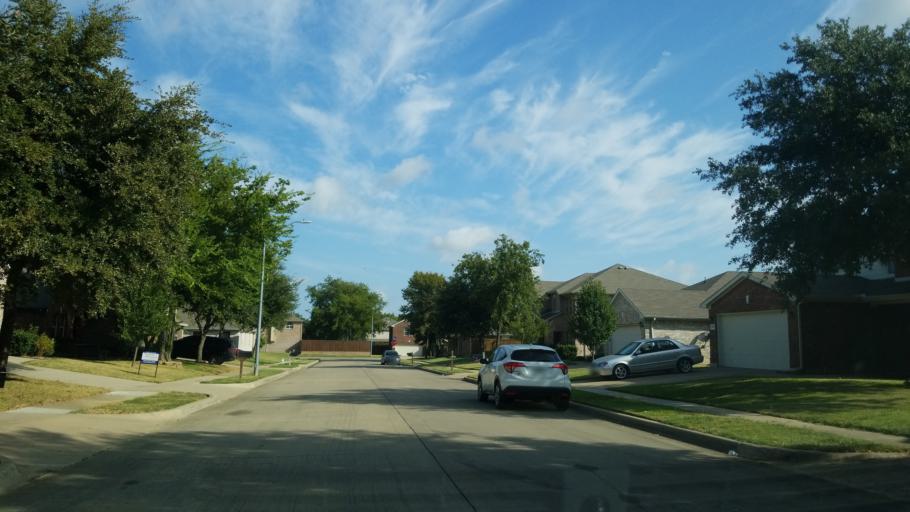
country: US
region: Texas
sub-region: Tarrant County
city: Euless
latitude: 32.8435
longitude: -97.0739
